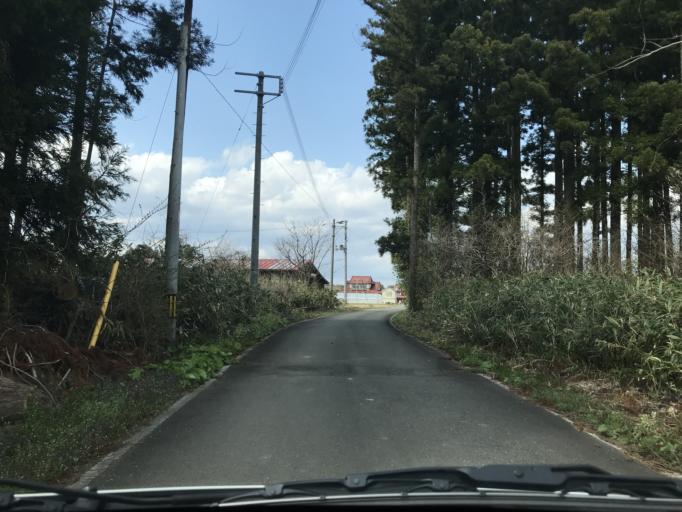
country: JP
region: Iwate
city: Mizusawa
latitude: 39.0754
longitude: 141.1016
